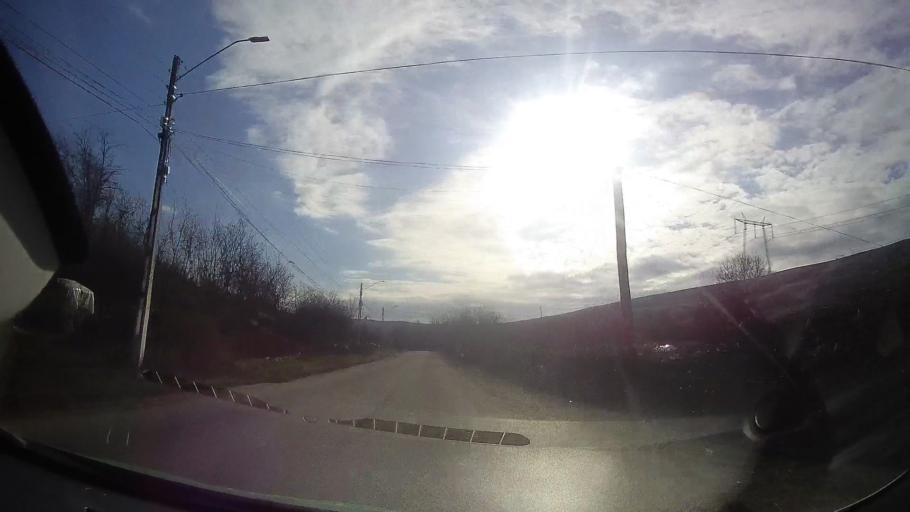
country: RO
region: Mures
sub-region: Comuna Valea Larga
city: Valea Larga
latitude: 46.6098
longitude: 24.0907
